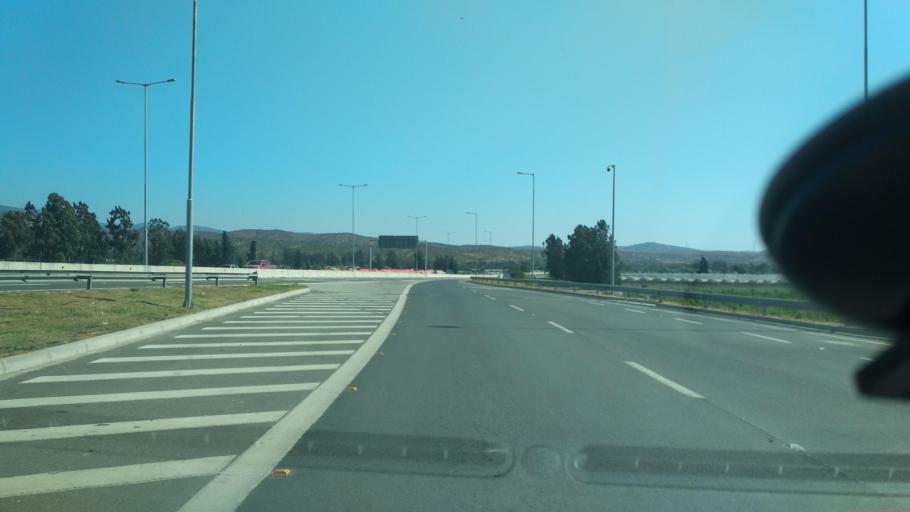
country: CL
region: Valparaiso
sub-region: Provincia de Marga Marga
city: Limache
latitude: -32.9735
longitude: -71.3028
